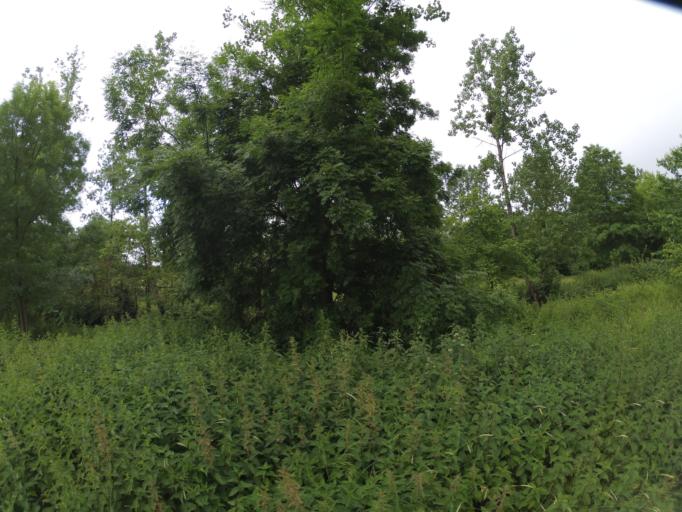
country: FR
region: Pays de la Loire
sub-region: Departement de la Vendee
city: Nesmy
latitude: 46.6256
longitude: -1.4196
